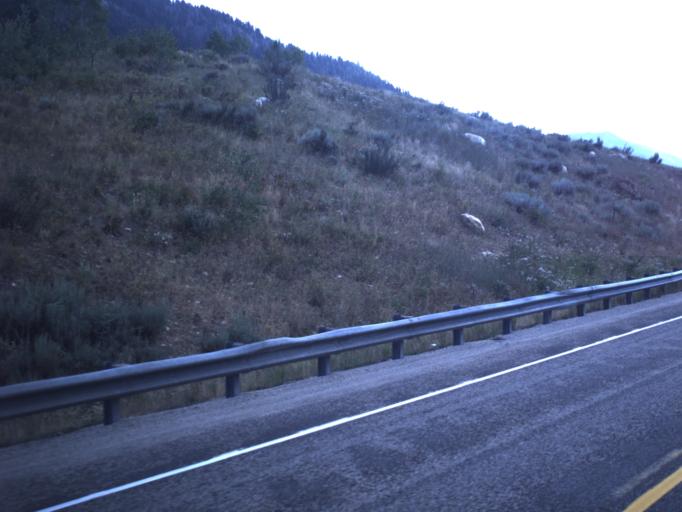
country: US
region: Utah
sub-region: Cache County
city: Richmond
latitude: 41.9080
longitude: -111.5627
